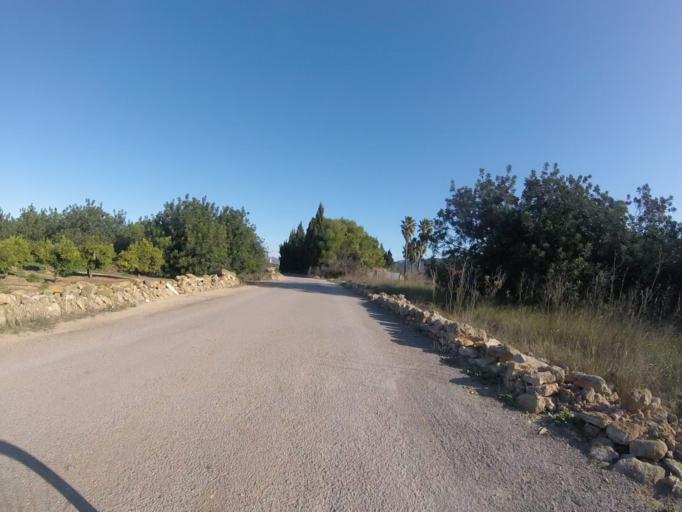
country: ES
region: Valencia
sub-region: Provincia de Castello
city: Alcala de Xivert
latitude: 40.2866
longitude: 0.2135
